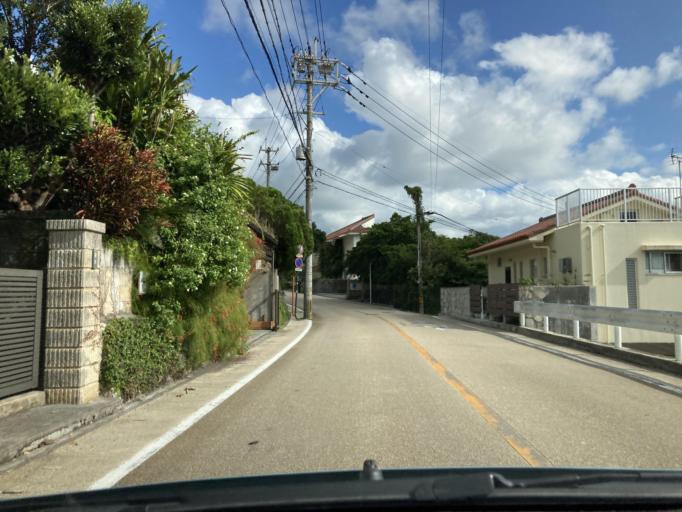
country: JP
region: Okinawa
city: Naha-shi
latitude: 26.2172
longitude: 127.7136
